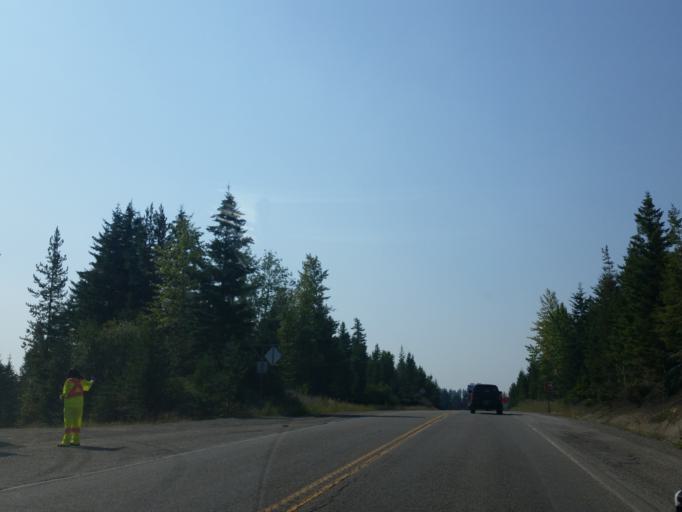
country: CA
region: British Columbia
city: Princeton
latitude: 49.2887
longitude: -120.5778
